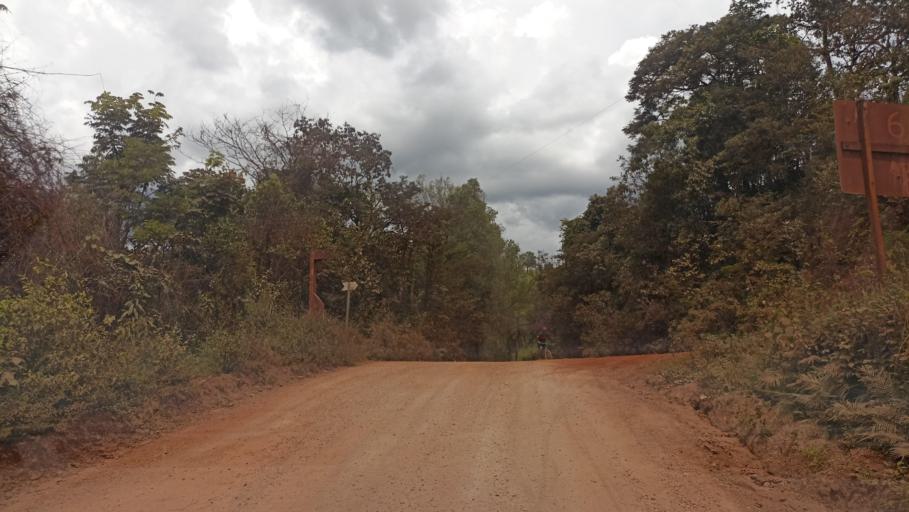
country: BR
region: Minas Gerais
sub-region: Itabirito
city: Itabirito
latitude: -20.3406
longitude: -43.7711
